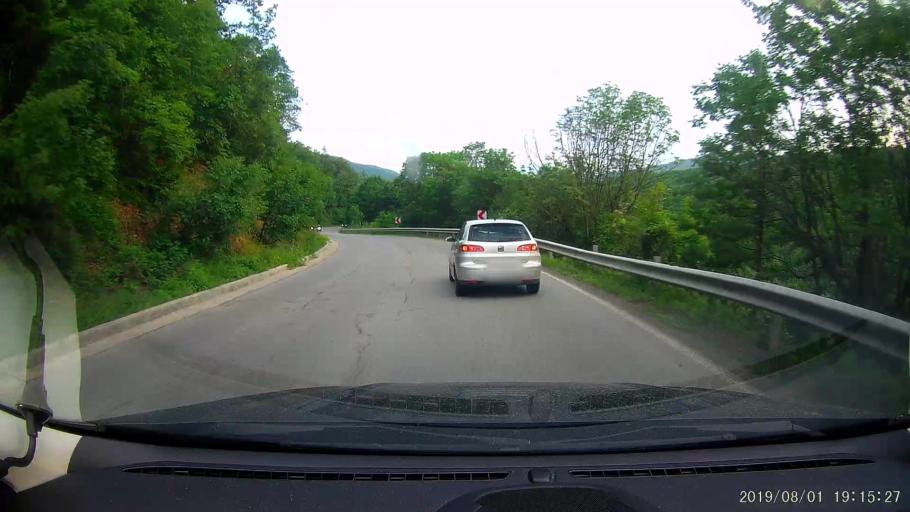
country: BG
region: Shumen
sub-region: Obshtina Smyadovo
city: Smyadovo
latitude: 42.9326
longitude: 26.9438
